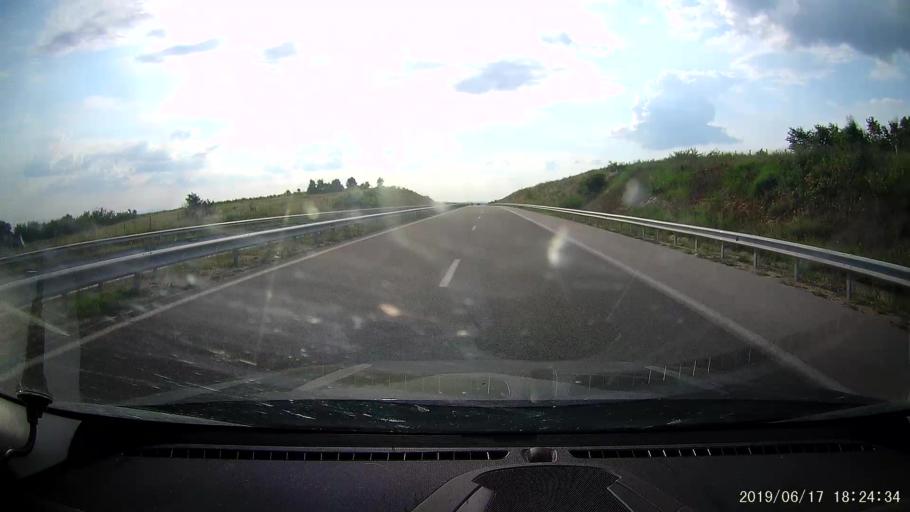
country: BG
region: Khaskovo
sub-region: Obshtina Dimitrovgrad
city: Dimitrovgrad
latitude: 41.9860
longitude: 25.6876
